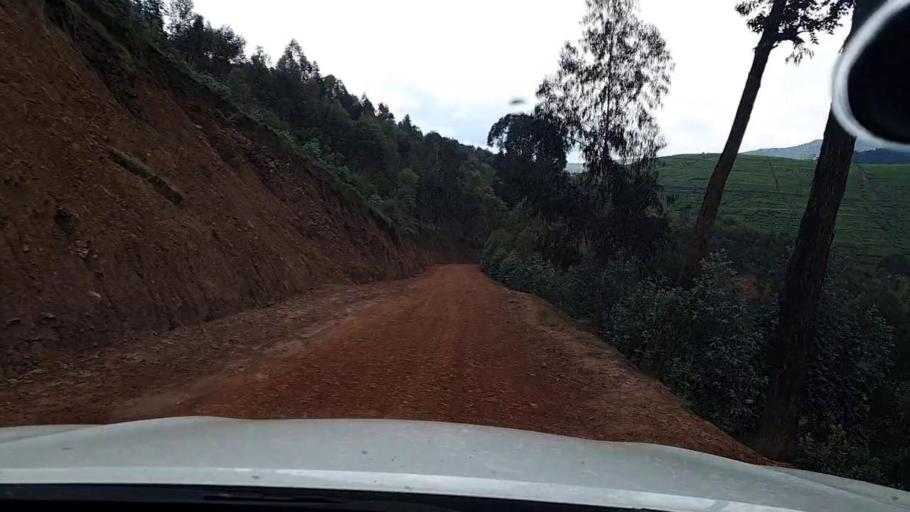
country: RW
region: Western Province
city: Kibuye
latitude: -2.1708
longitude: 29.4352
